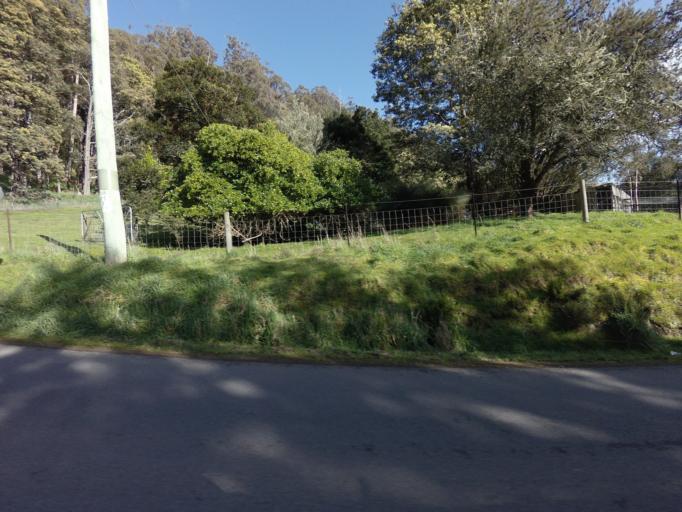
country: AU
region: Tasmania
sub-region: Huon Valley
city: Geeveston
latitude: -43.2483
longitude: 146.9907
